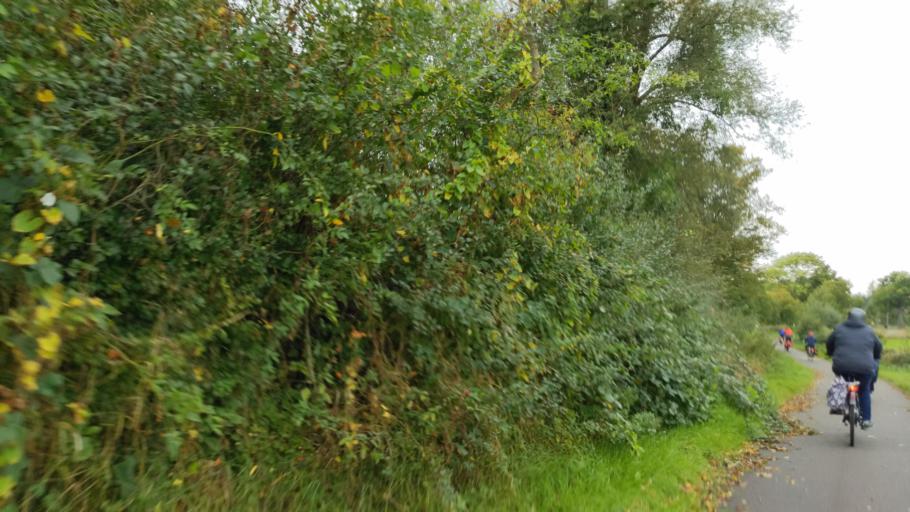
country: DE
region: Schleswig-Holstein
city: Gross Sarau
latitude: 53.7660
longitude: 10.7724
